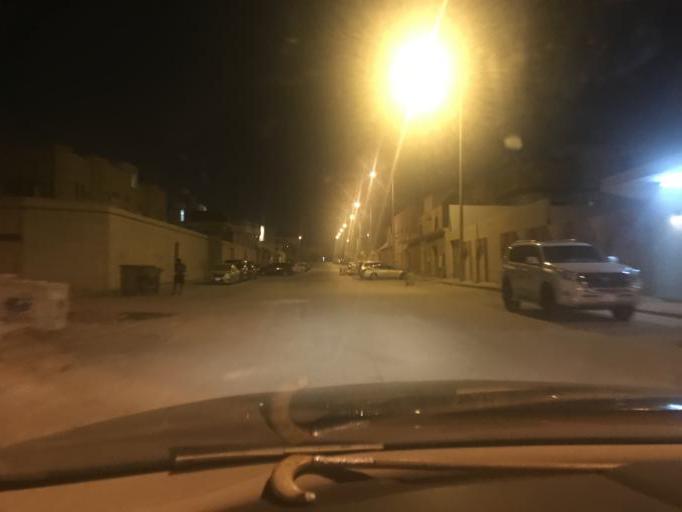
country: SA
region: Ar Riyad
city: Riyadh
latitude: 24.7568
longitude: 46.7628
